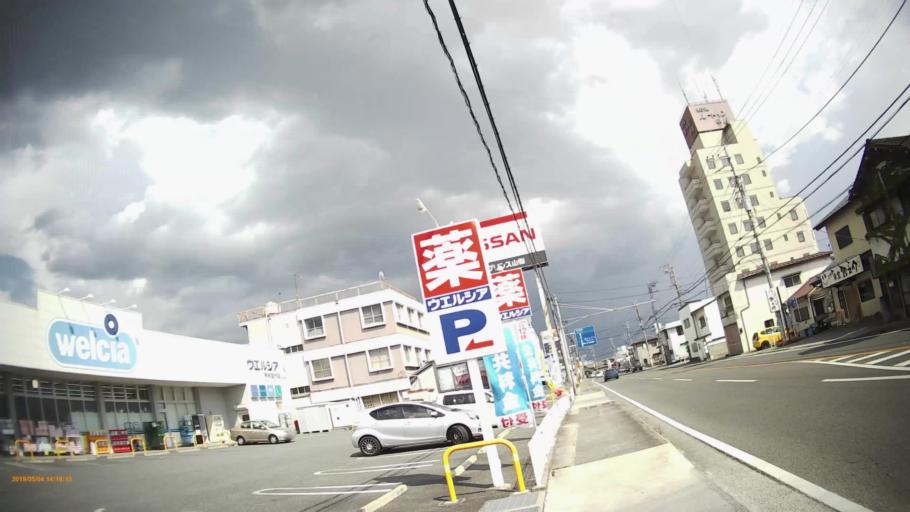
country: JP
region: Yamanashi
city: Kofu-shi
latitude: 35.6593
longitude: 138.5456
